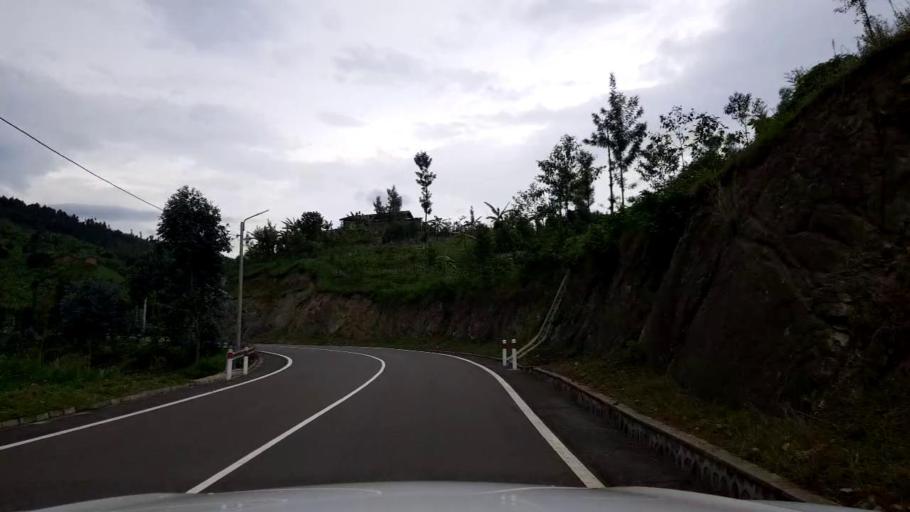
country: RW
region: Western Province
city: Kibuye
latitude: -2.0297
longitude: 29.3945
